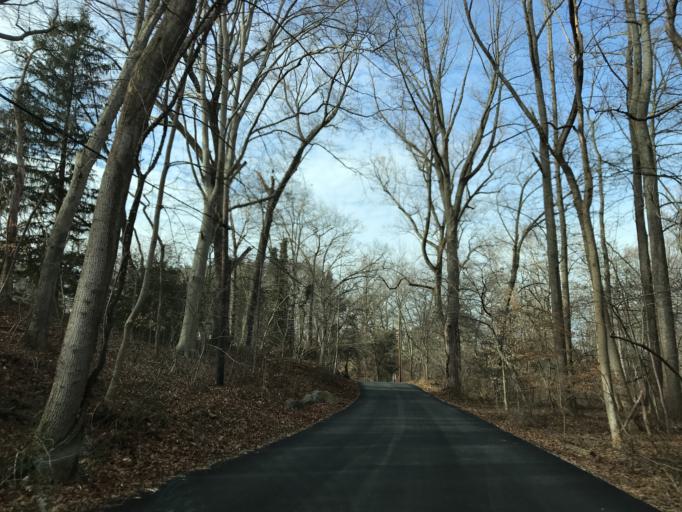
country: US
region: Maryland
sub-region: Harford County
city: Pleasant Hills
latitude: 39.4522
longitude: -76.3881
